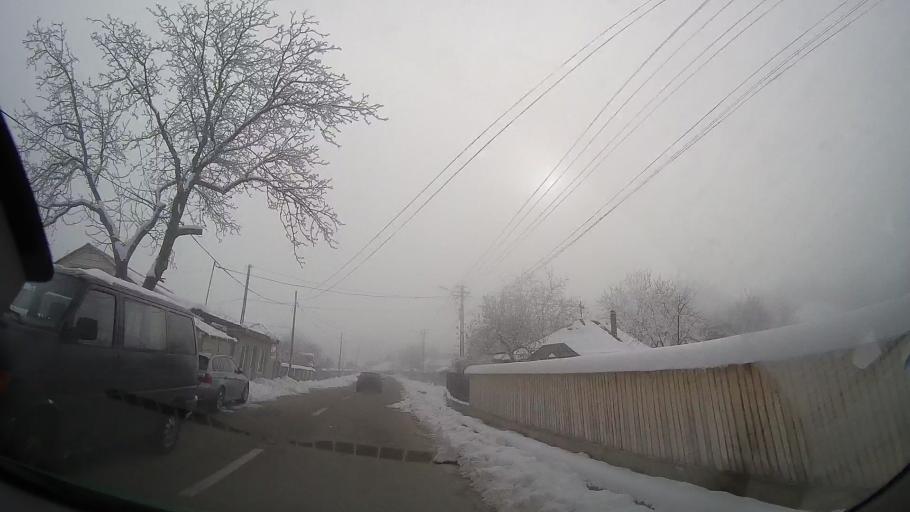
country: RO
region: Iasi
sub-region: Comuna Valea Seaca
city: Valea Seaca
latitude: 47.2889
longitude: 26.6668
